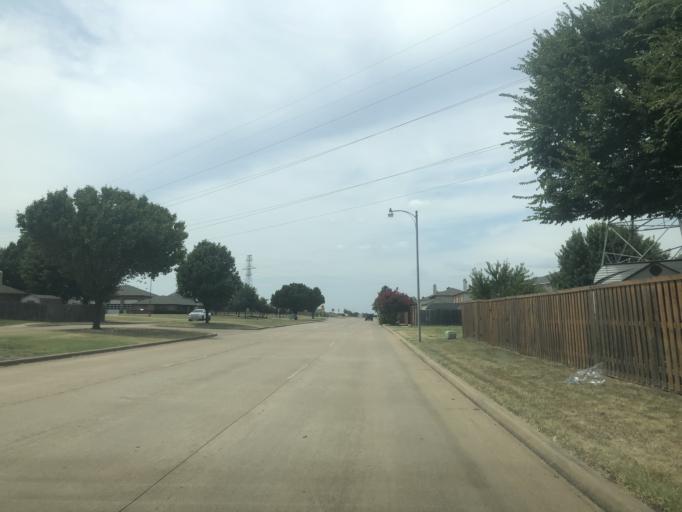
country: US
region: Texas
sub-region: Tarrant County
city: Saginaw
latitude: 32.8750
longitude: -97.3501
